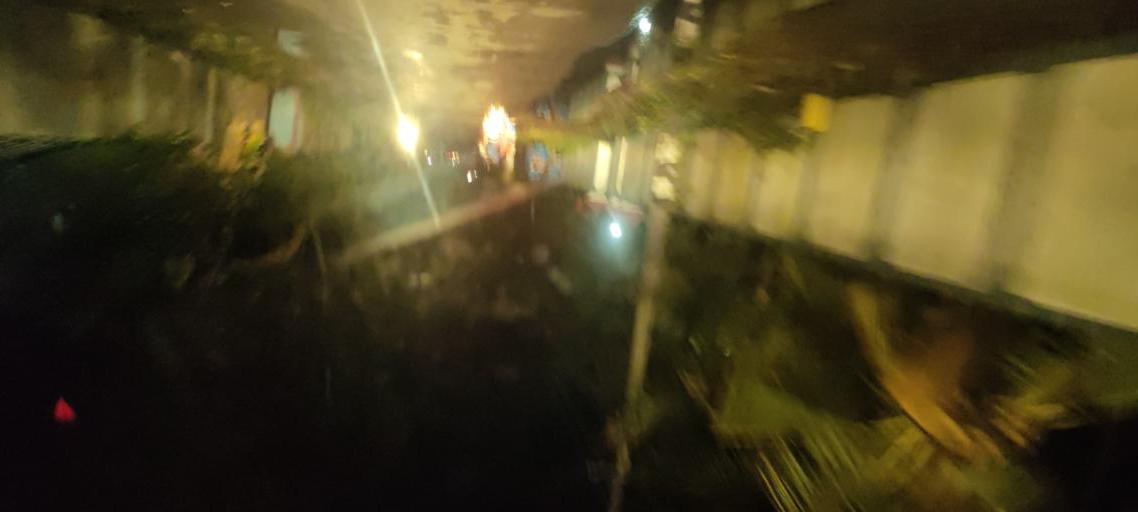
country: IN
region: Kerala
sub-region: Alappuzha
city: Vayalar
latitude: 9.7229
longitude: 76.3266
